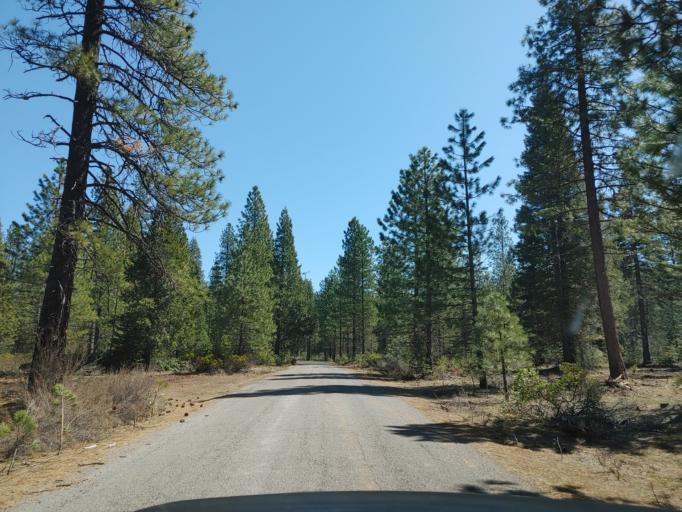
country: US
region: California
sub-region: Siskiyou County
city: McCloud
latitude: 41.2444
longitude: -121.9660
